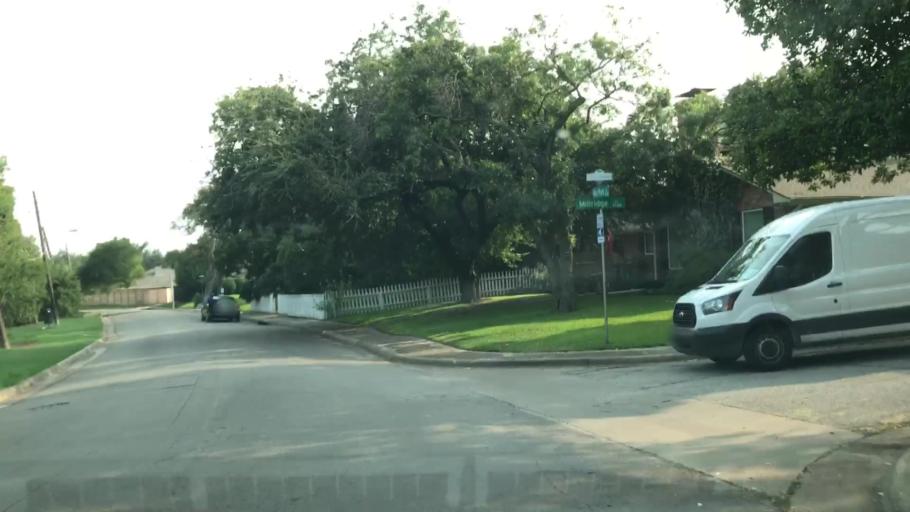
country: US
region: Texas
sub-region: Dallas County
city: Richardson
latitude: 32.9040
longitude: -96.7286
